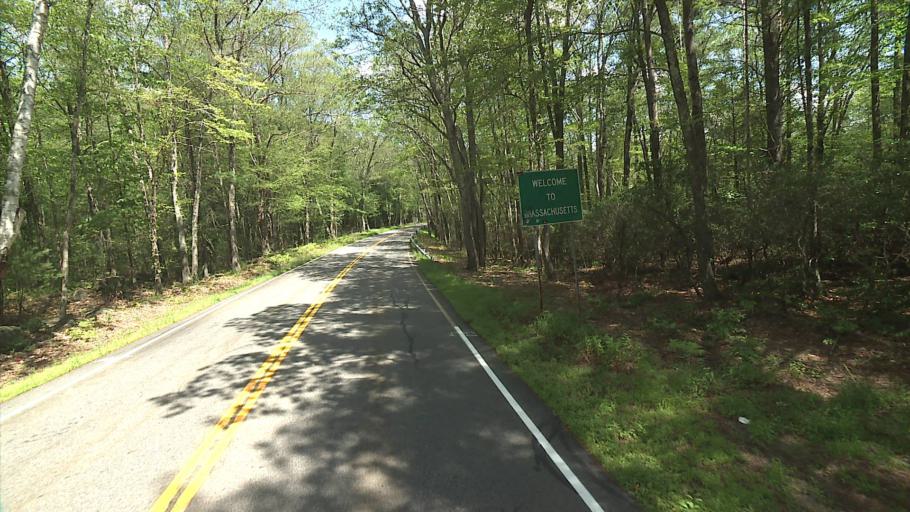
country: US
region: Massachusetts
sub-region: Worcester County
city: Southbridge
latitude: 42.0279
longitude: -72.0718
